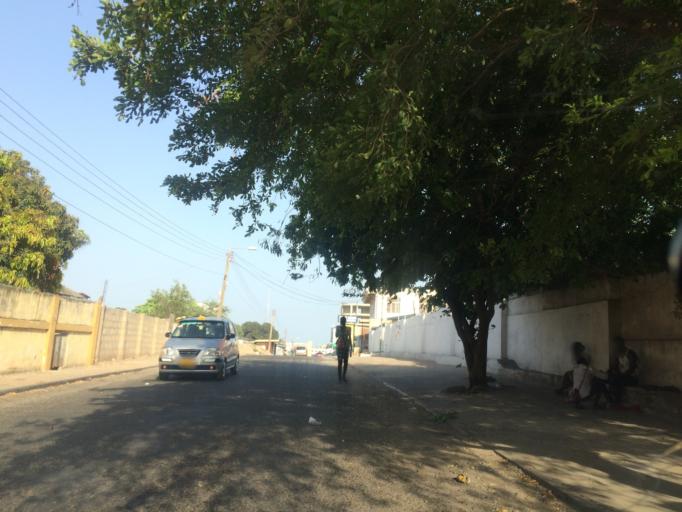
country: GH
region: Greater Accra
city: Accra
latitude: 5.5613
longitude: -0.1858
